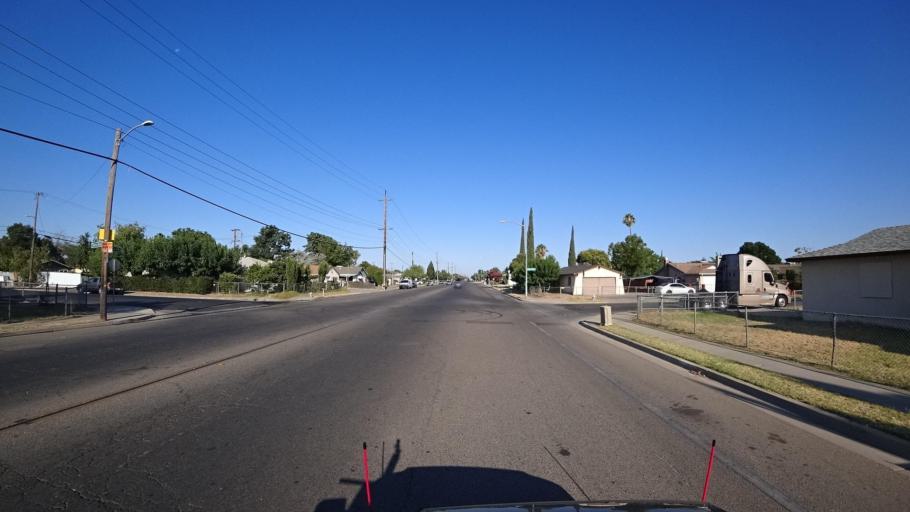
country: US
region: California
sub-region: Fresno County
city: Fresno
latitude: 36.7142
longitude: -119.7413
